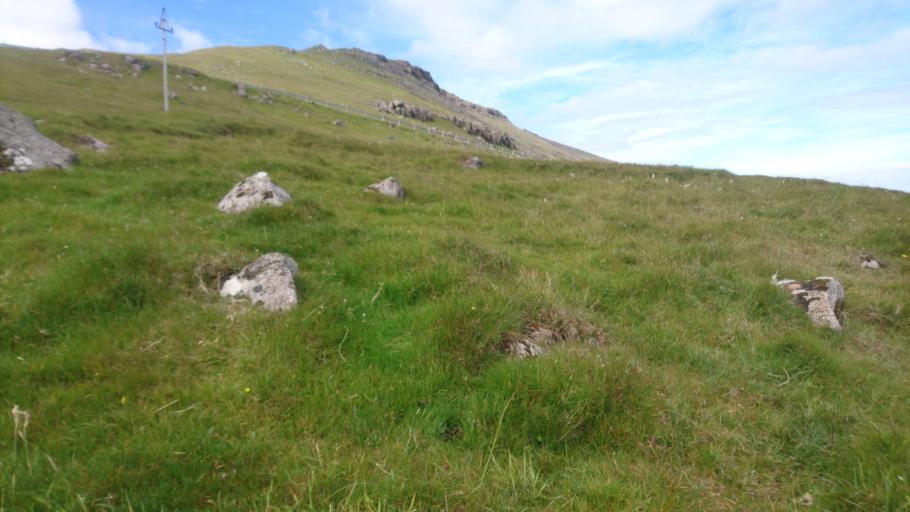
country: FO
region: Nordoyar
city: Klaksvik
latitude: 62.3229
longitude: -6.2848
